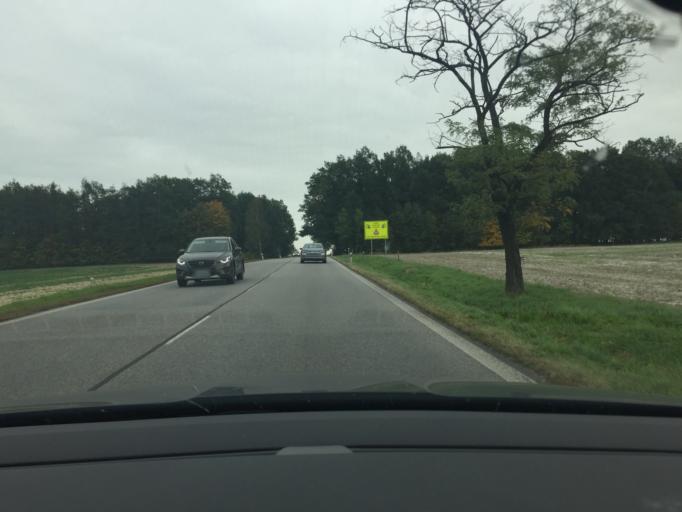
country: CZ
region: Jihocesky
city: Zliv
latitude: 49.0296
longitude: 14.3721
